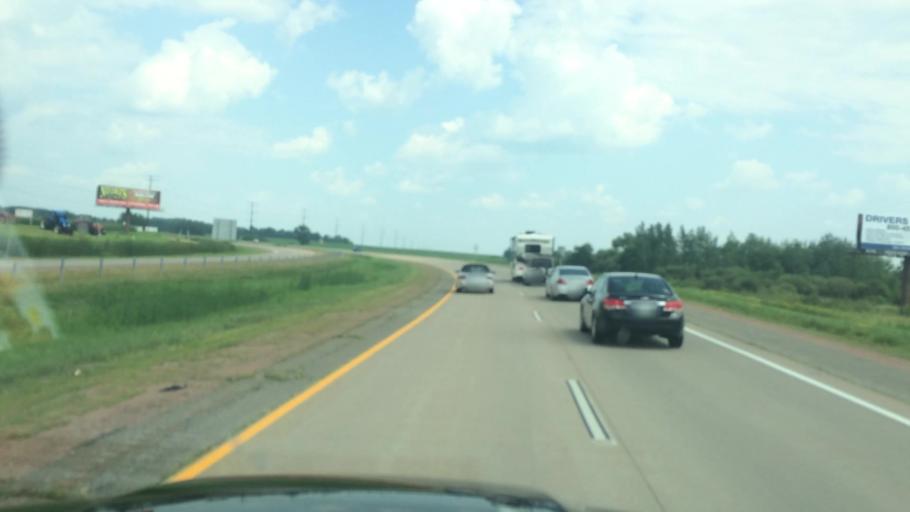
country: US
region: Wisconsin
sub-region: Clark County
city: Abbotsford
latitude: 44.9326
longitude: -90.3020
